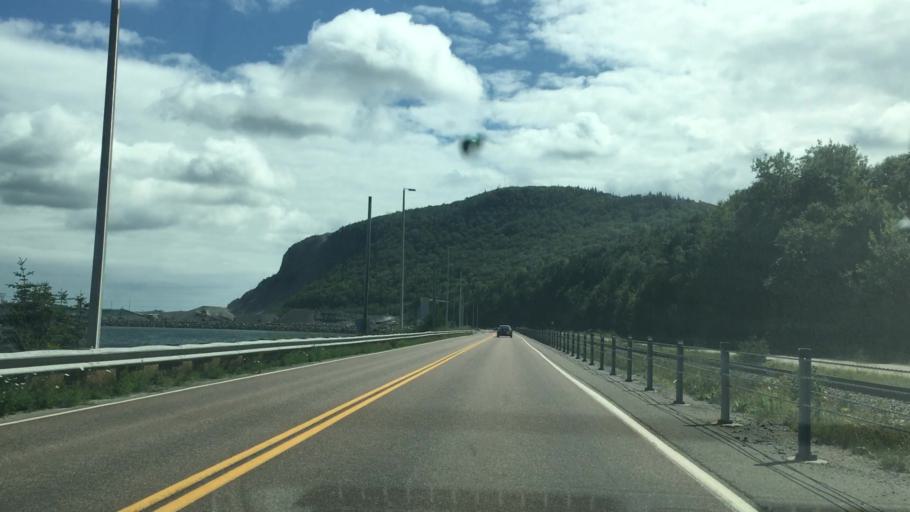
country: CA
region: Nova Scotia
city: Port Hawkesbury
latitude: 45.6444
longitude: -61.4334
